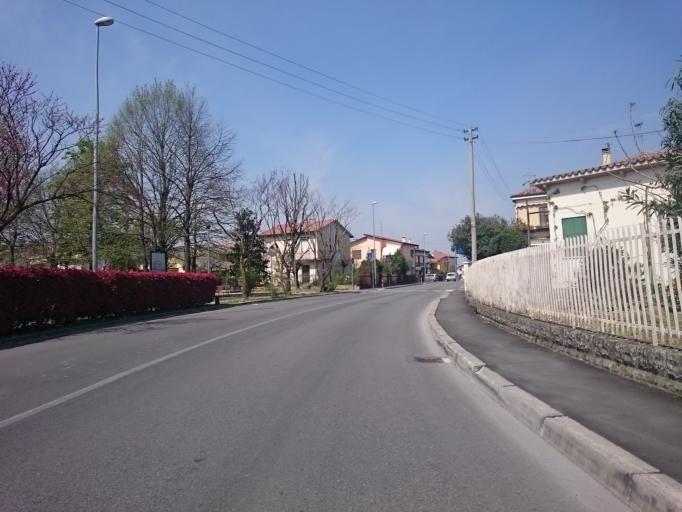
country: IT
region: Veneto
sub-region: Provincia di Padova
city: Tencarola
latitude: 45.3960
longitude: 11.8063
